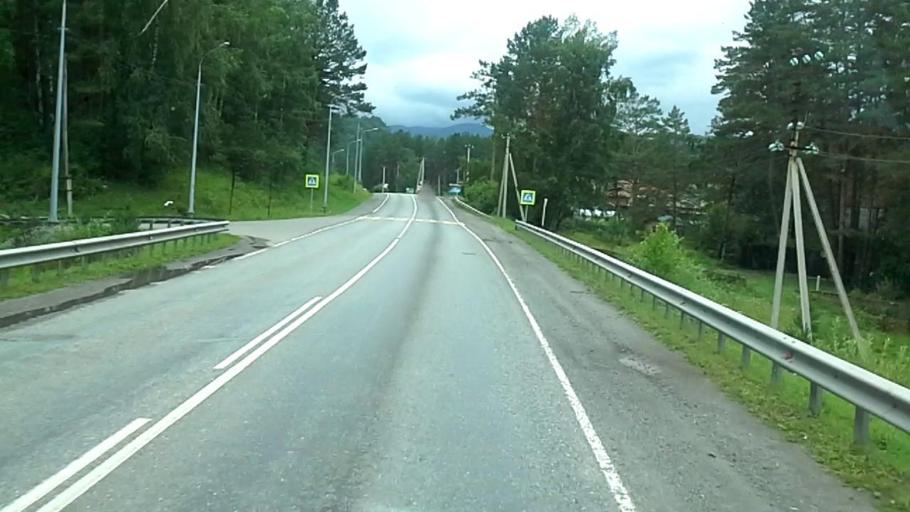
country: RU
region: Altay
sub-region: Mayminskiy Rayon
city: Manzherok
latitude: 51.8184
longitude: 85.7812
